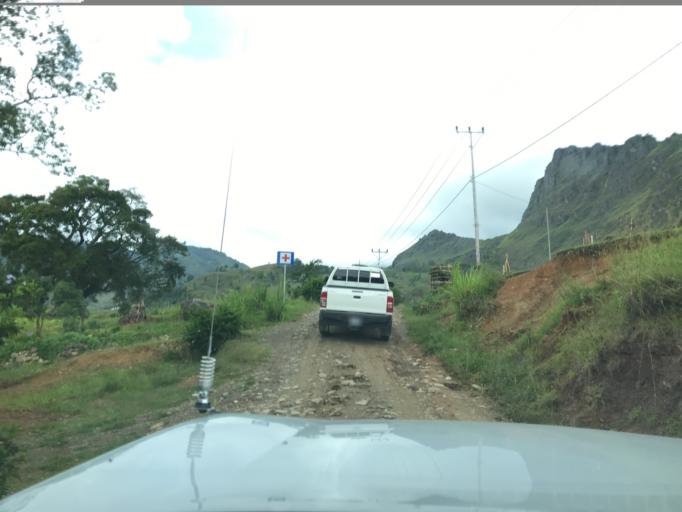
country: TL
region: Aileu
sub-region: Aileu Villa
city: Aileu
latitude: -8.8528
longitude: 125.5818
